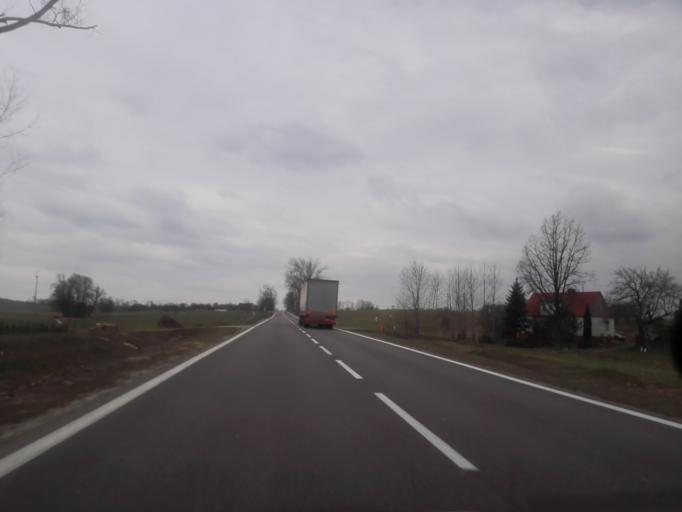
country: PL
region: Podlasie
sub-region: Powiat augustowski
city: Augustow
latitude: 53.7961
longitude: 22.8764
